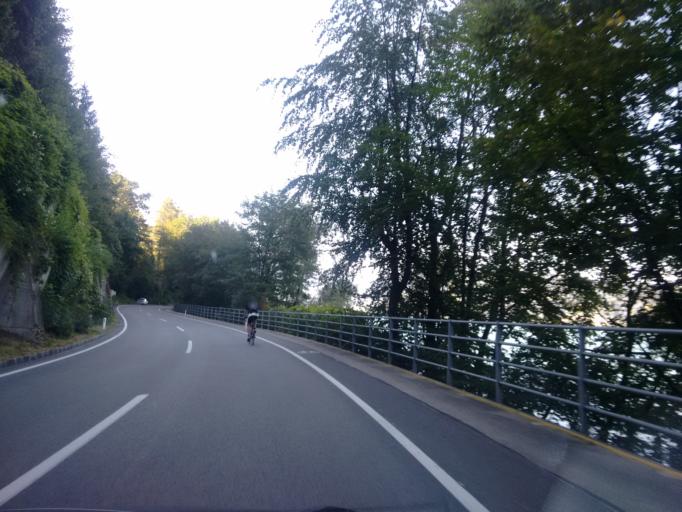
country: AT
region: Upper Austria
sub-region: Politischer Bezirk Vocklabruck
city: Steinbach am Attersee
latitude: 47.8468
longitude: 13.5504
